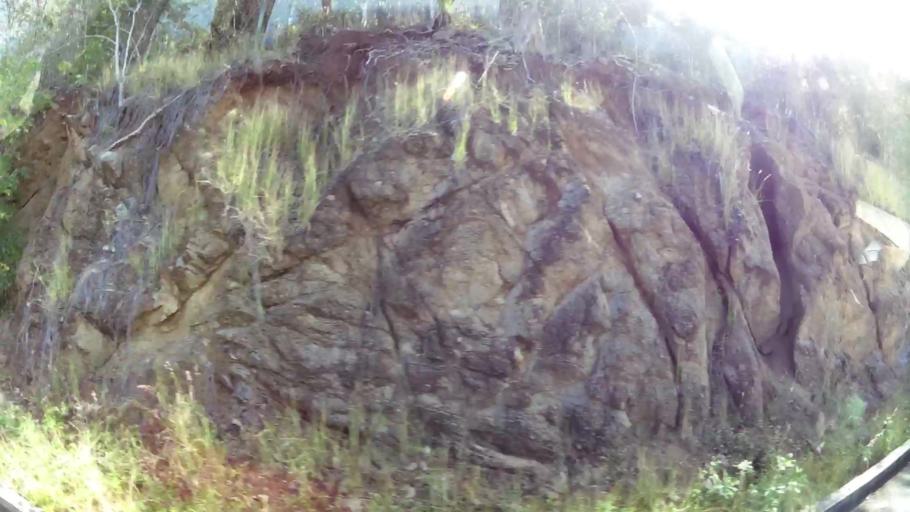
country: VG
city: Tortola
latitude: 18.4971
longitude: -64.4071
